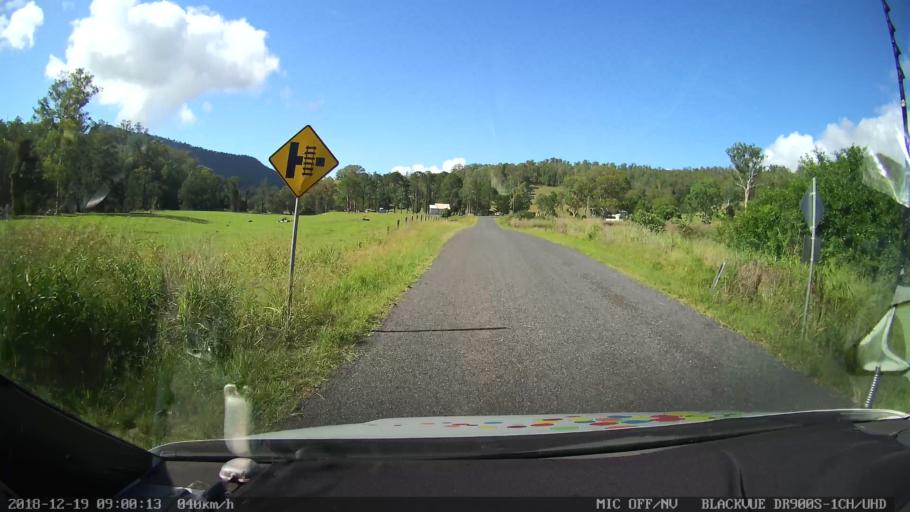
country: AU
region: New South Wales
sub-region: Kyogle
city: Kyogle
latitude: -28.4303
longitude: 152.9577
